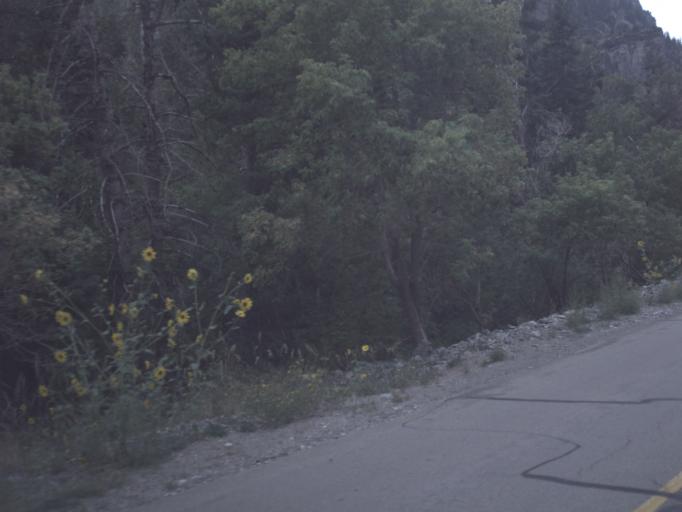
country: US
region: Utah
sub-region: Utah County
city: Cedar Hills
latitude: 40.4467
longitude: -111.6905
